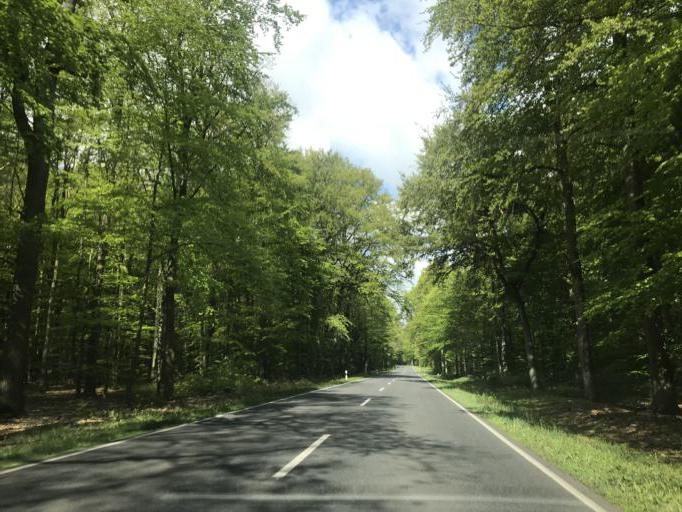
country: DE
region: Brandenburg
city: Marienwerder
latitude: 52.8607
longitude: 13.5260
